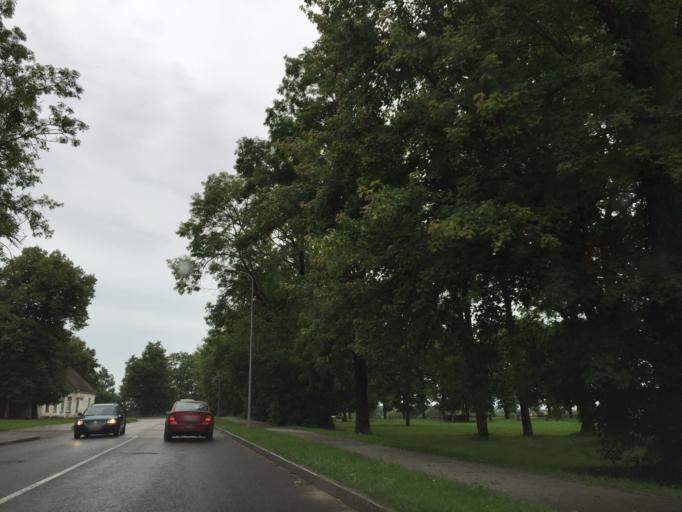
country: LV
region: Jekabpils Rajons
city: Jekabpils
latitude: 56.5133
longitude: 25.8575
